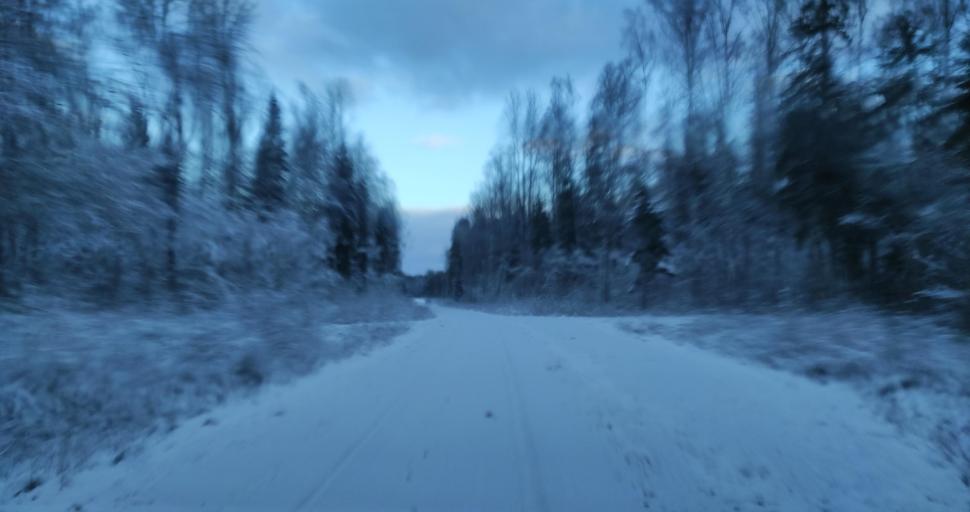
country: LV
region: Skrunda
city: Skrunda
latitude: 56.5773
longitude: 21.9202
